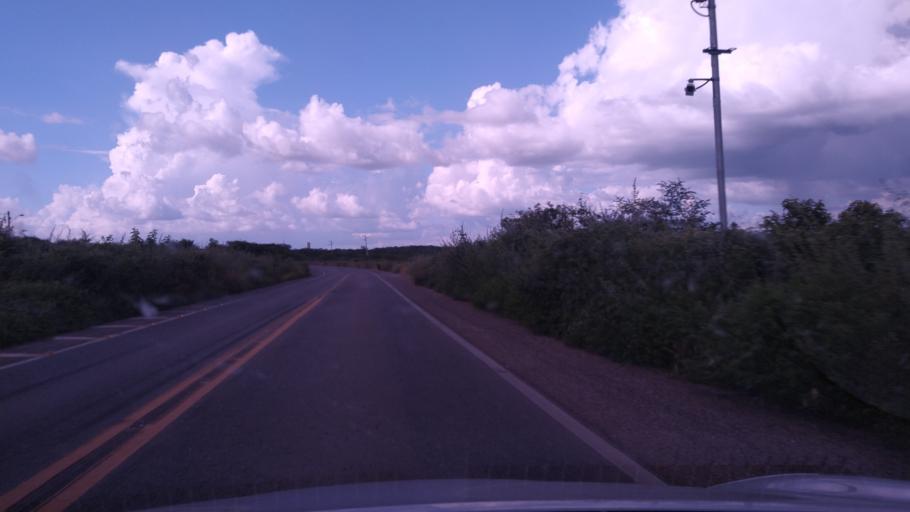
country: BR
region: Ceara
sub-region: Caninde
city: Caninde
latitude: -4.3962
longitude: -39.3157
